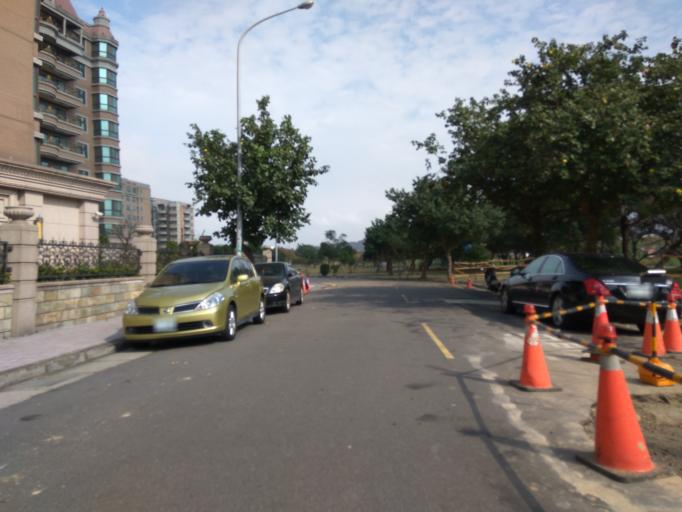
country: TW
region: Taiwan
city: Taoyuan City
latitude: 25.0170
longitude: 121.2240
